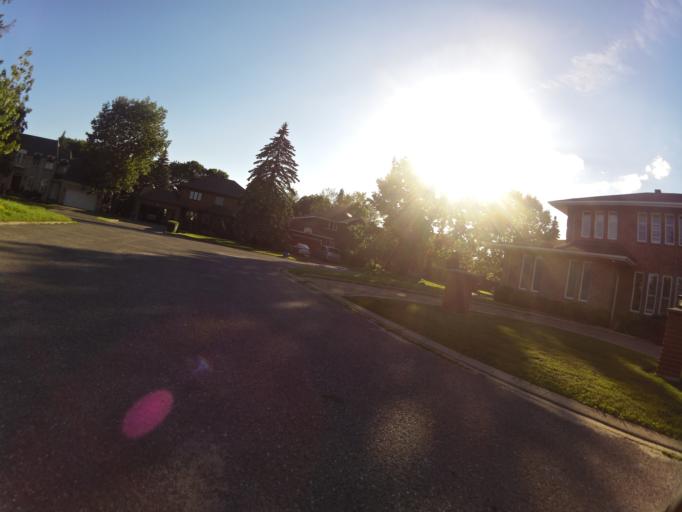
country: CA
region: Ontario
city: Bells Corners
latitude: 45.3324
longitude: -75.7641
